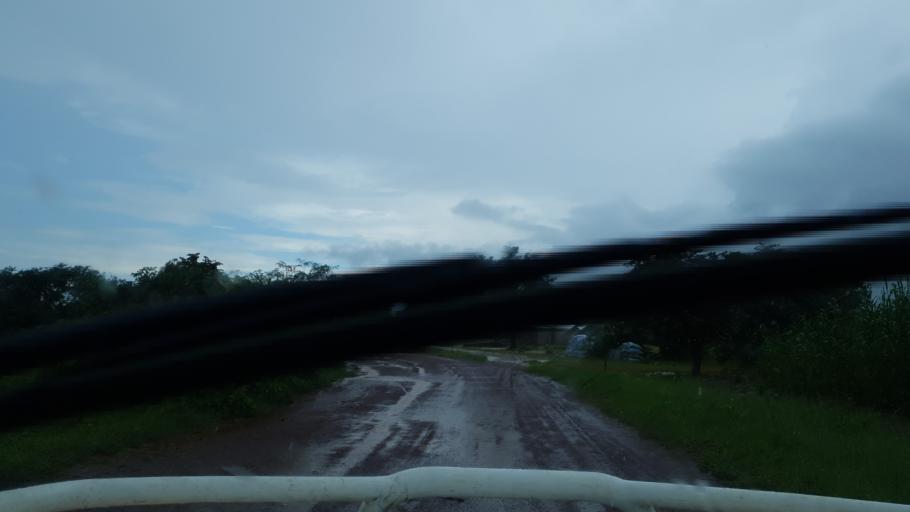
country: ML
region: Sikasso
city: Kolondieba
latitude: 11.5963
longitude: -6.6644
